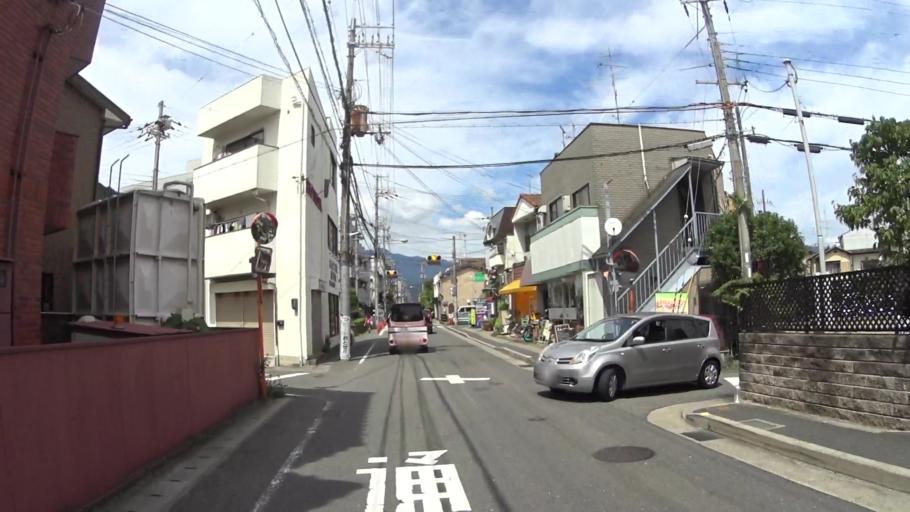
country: JP
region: Kyoto
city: Muko
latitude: 35.0028
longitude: 135.6859
